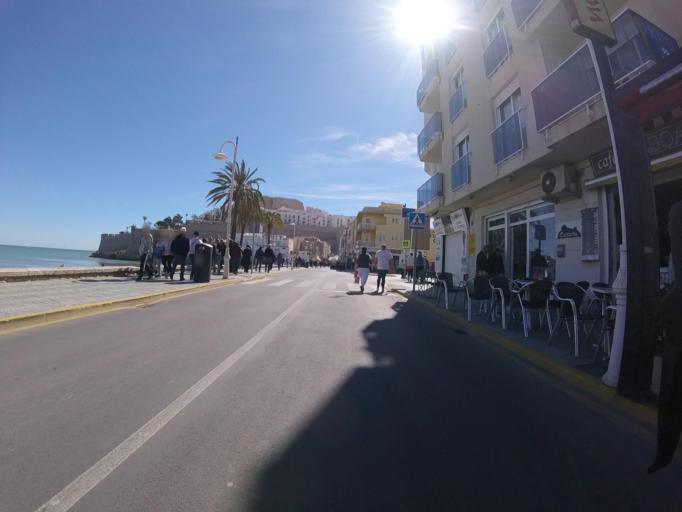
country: ES
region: Valencia
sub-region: Provincia de Castello
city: Peniscola
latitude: 40.3596
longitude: 0.4043
